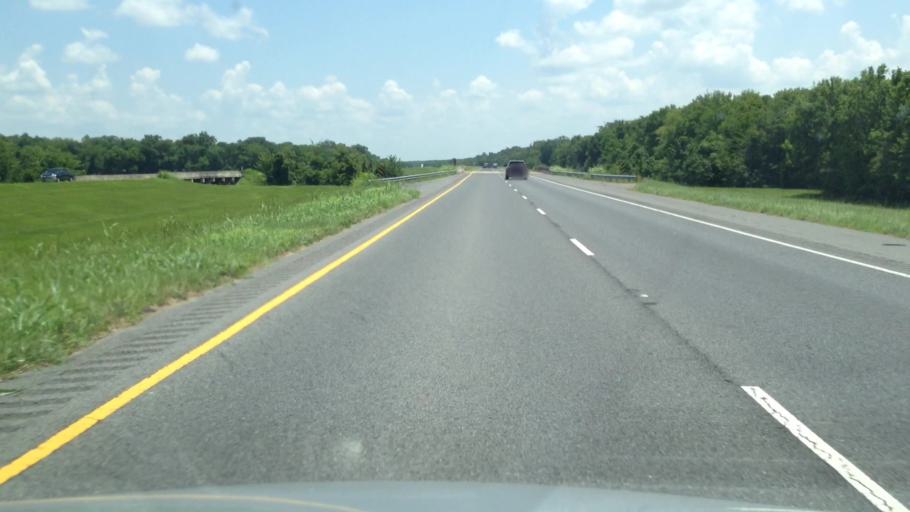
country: US
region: Louisiana
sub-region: Avoyelles Parish
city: Bunkie
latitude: 30.8225
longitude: -92.2235
